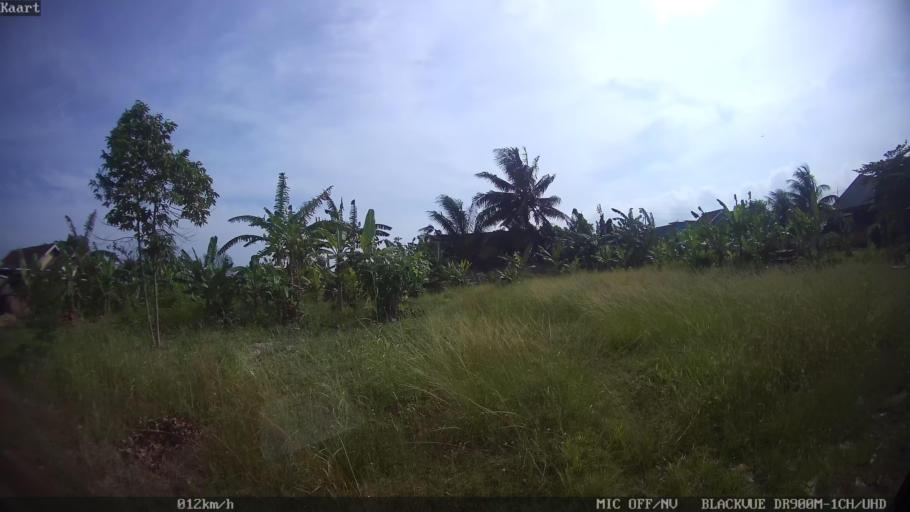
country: ID
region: Lampung
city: Kedaton
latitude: -5.3767
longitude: 105.2977
